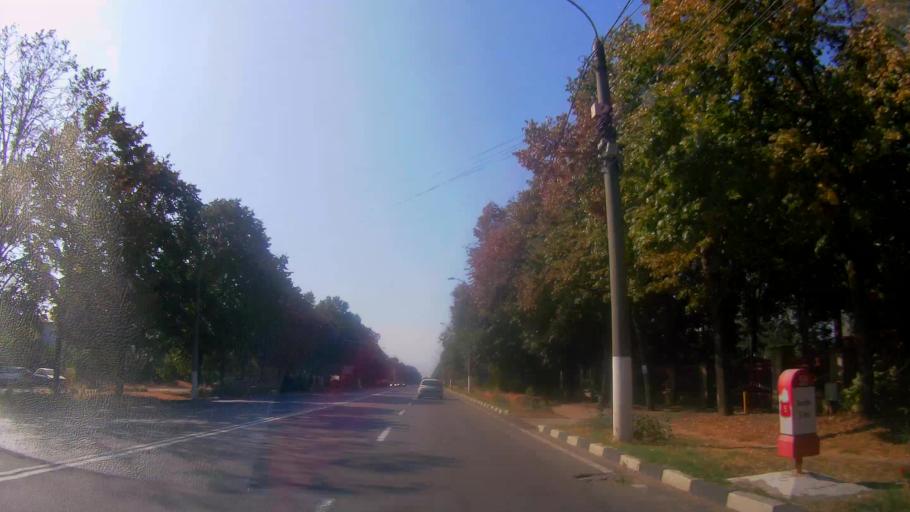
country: RO
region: Giurgiu
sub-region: Comuna Fratesti
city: Remus
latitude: 43.9309
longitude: 25.9758
